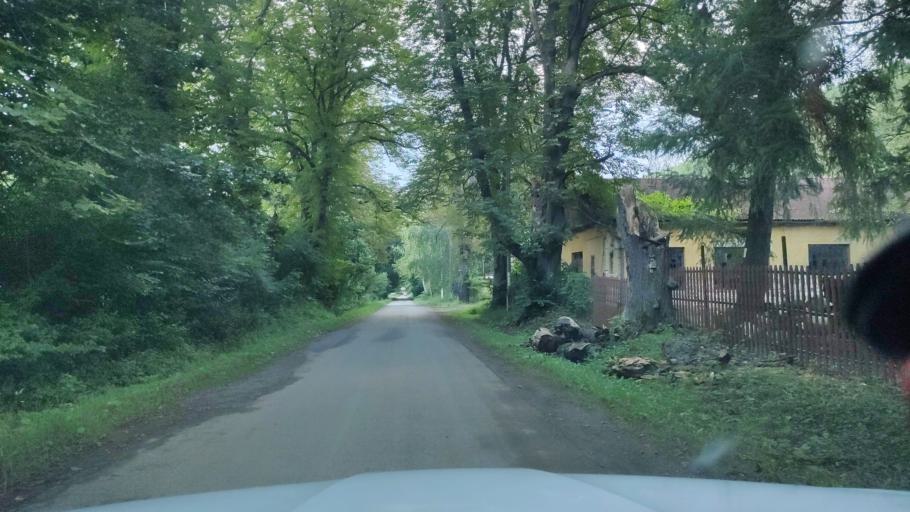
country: HU
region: Heves
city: Parad
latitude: 47.9079
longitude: 20.0561
